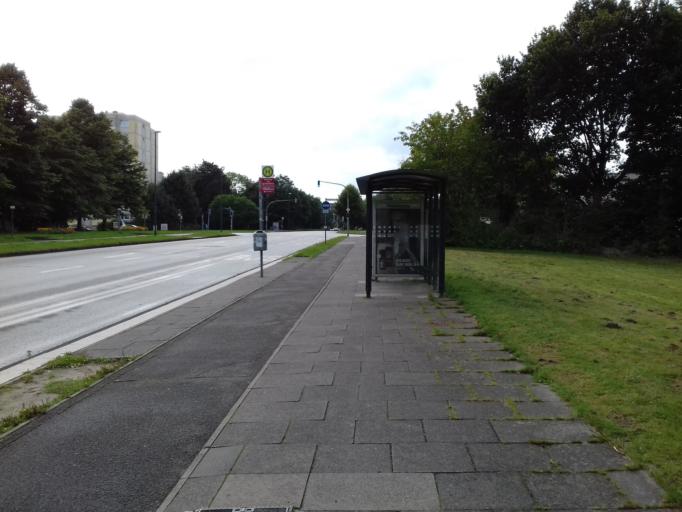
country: DE
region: Schleswig-Holstein
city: Kronshagen
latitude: 54.3254
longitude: 10.0645
